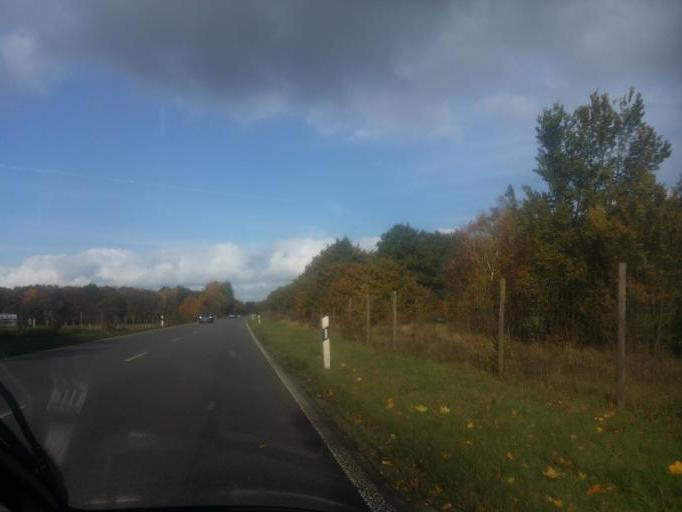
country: DE
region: Schleswig-Holstein
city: Pinneberg
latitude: 53.6307
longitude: 9.7765
